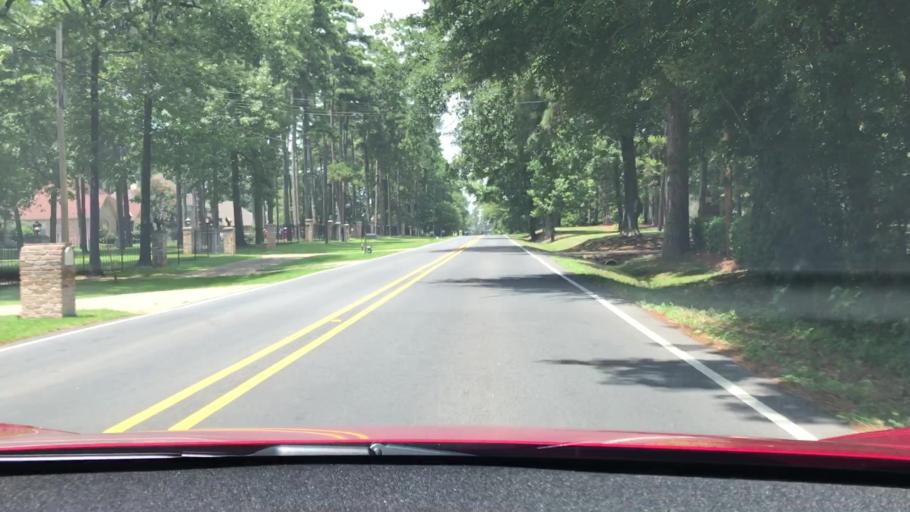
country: US
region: Louisiana
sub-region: Bossier Parish
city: Bossier City
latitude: 32.3789
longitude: -93.7138
